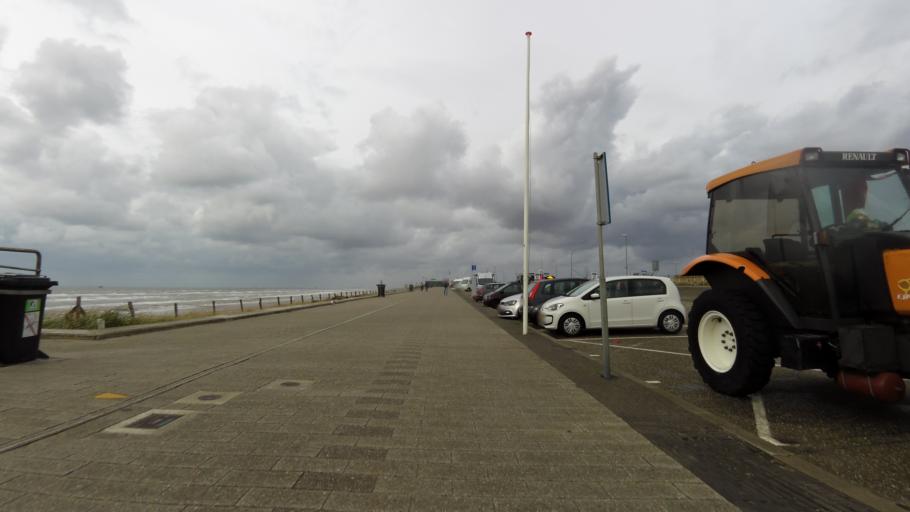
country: NL
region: North Holland
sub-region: Gemeente Zandvoort
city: Zandvoort
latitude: 52.3863
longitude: 4.5337
